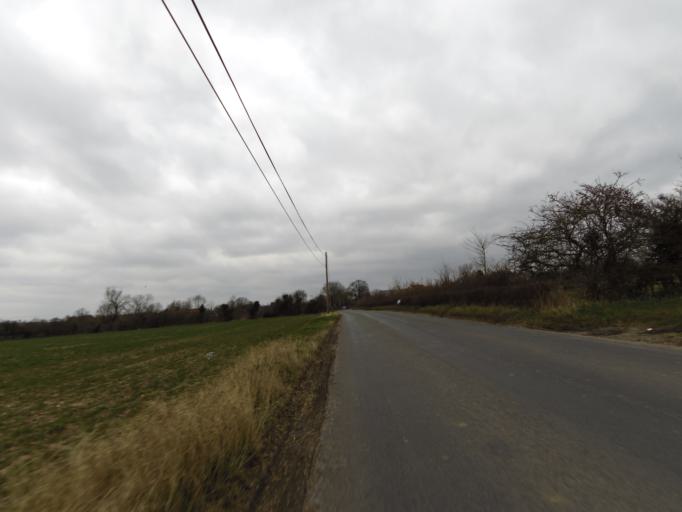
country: GB
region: England
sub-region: Suffolk
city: Ipswich
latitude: 52.1317
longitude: 1.1662
